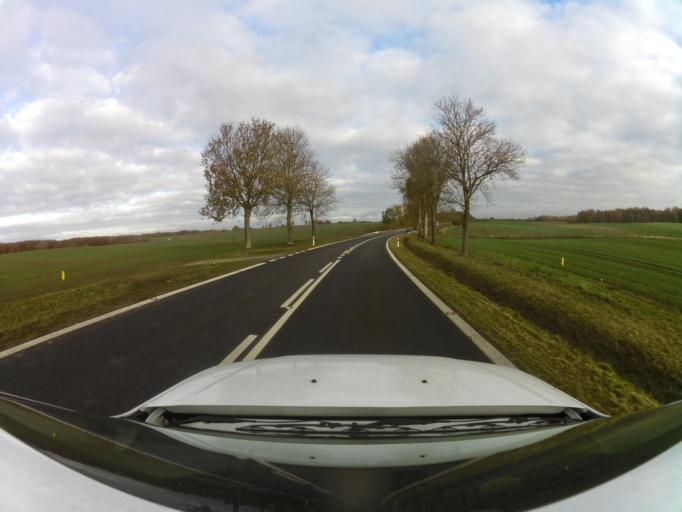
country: PL
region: West Pomeranian Voivodeship
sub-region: Powiat gryficki
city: Trzebiatow
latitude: 54.0290
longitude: 15.2408
